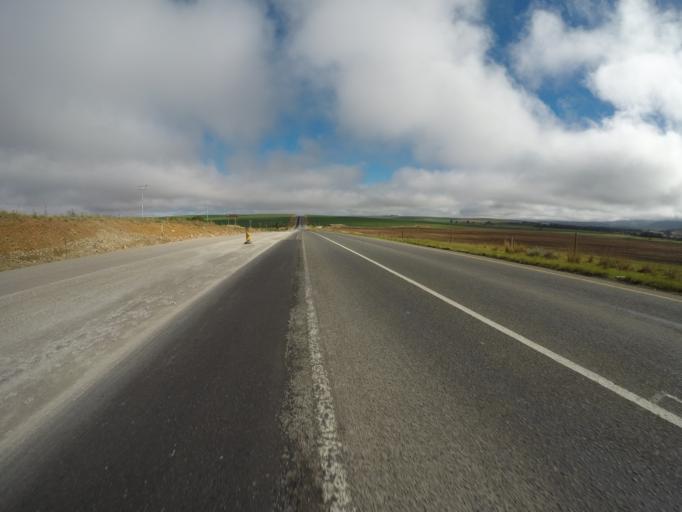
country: ZA
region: Western Cape
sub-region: Cape Winelands District Municipality
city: Ashton
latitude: -34.1541
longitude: 19.8910
